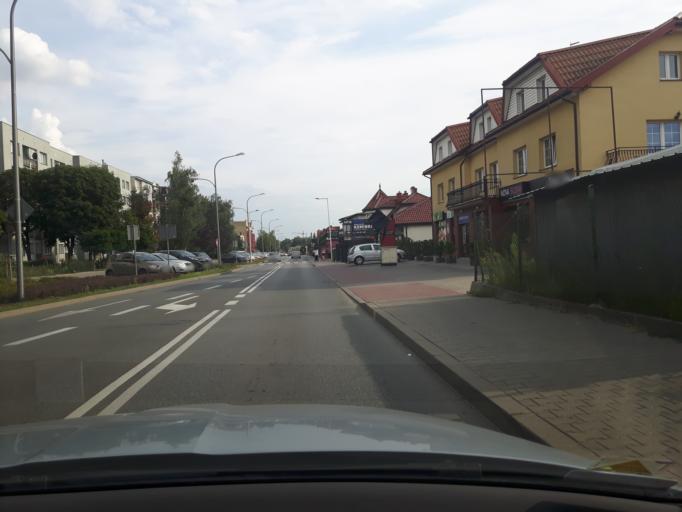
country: PL
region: Masovian Voivodeship
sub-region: Powiat piaseczynski
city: Piaseczno
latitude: 52.0788
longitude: 21.0158
